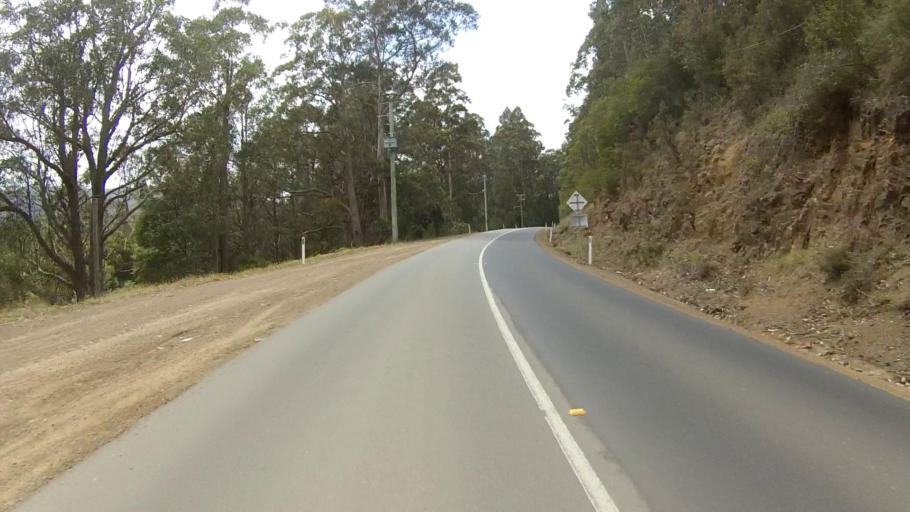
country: AU
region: Tasmania
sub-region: Huon Valley
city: Cygnet
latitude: -43.1311
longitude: 147.1572
